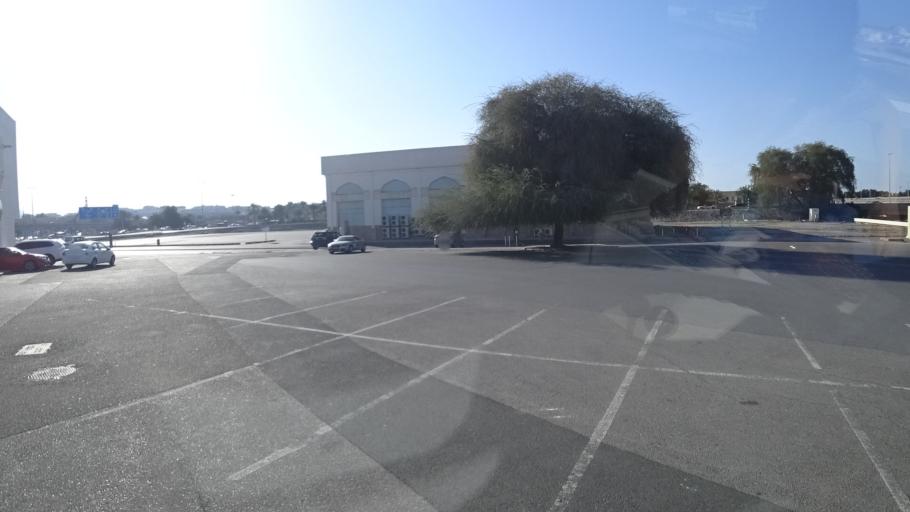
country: OM
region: Muhafazat Masqat
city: Muscat
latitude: 23.6139
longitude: 58.4950
